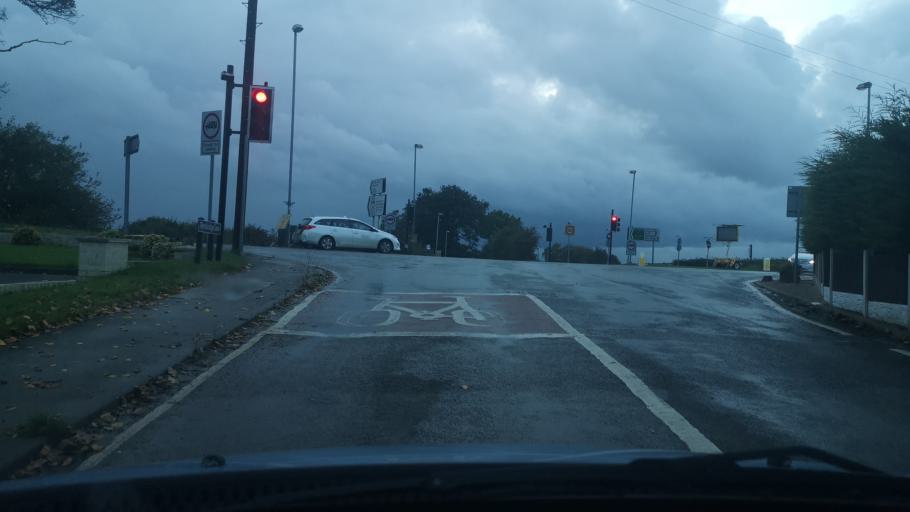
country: GB
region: England
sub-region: City and Borough of Wakefield
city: Badsworth
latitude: 53.6415
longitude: -1.2774
